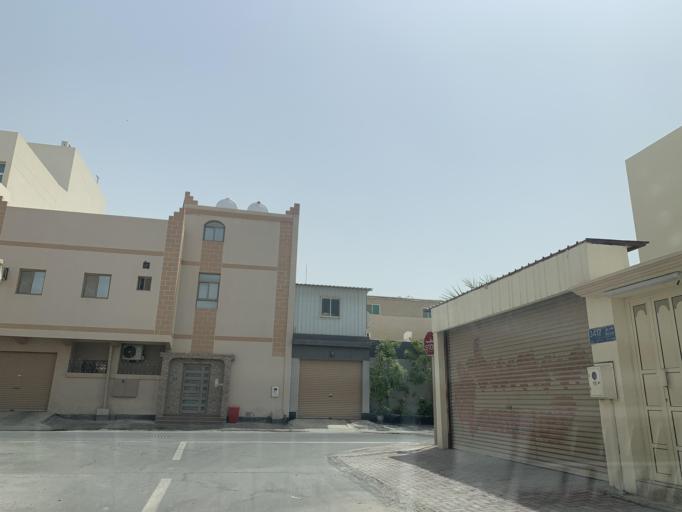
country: BH
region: Northern
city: Madinat `Isa
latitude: 26.1567
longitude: 50.5248
